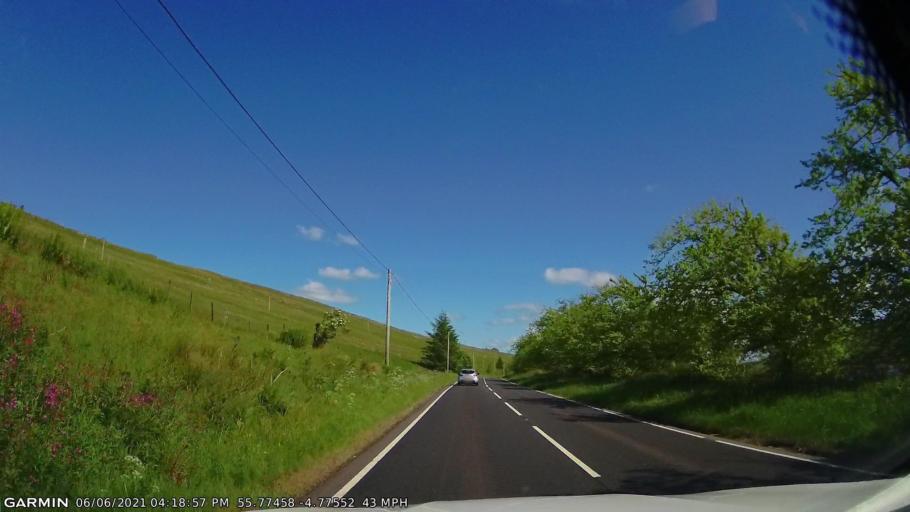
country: GB
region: Scotland
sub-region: North Ayrshire
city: Fairlie
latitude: 55.7746
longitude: -4.7755
